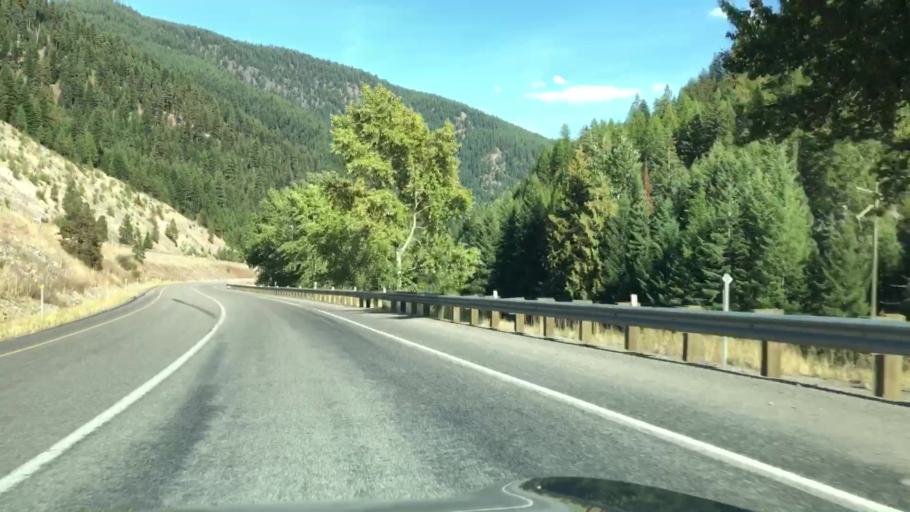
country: US
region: Montana
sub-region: Sanders County
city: Thompson Falls
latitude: 47.3127
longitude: -115.2321
